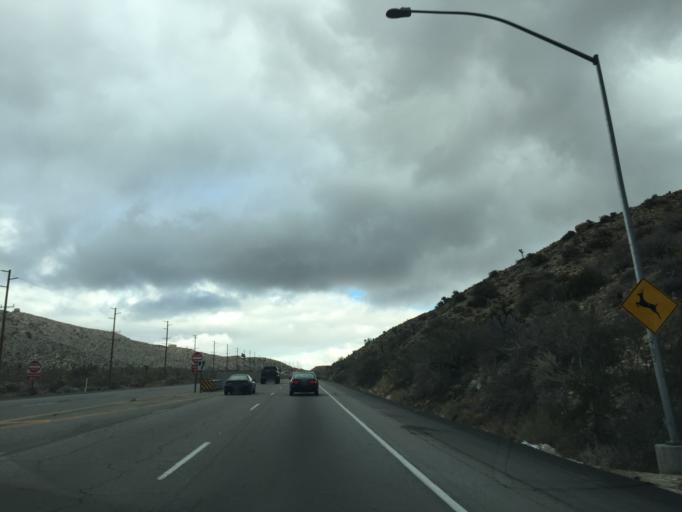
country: US
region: California
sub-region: San Bernardino County
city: Yucca Valley
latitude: 34.1035
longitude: -116.4928
